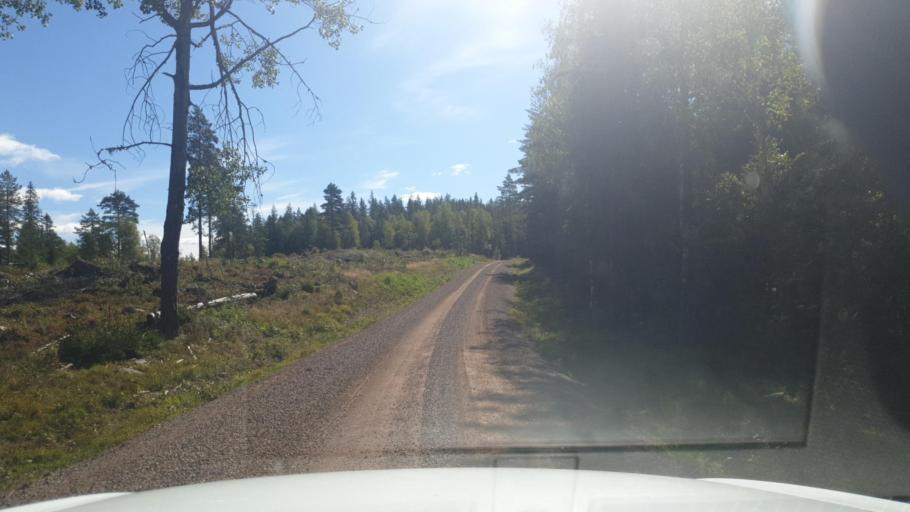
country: SE
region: Vaermland
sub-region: Eda Kommun
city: Charlottenberg
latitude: 60.0468
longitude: 12.5738
